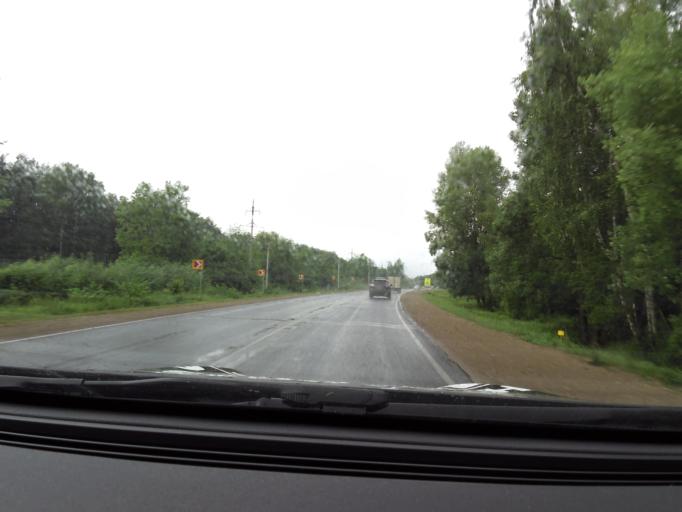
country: RU
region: Bashkortostan
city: Mikhaylovka
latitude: 54.8399
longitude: 55.7925
